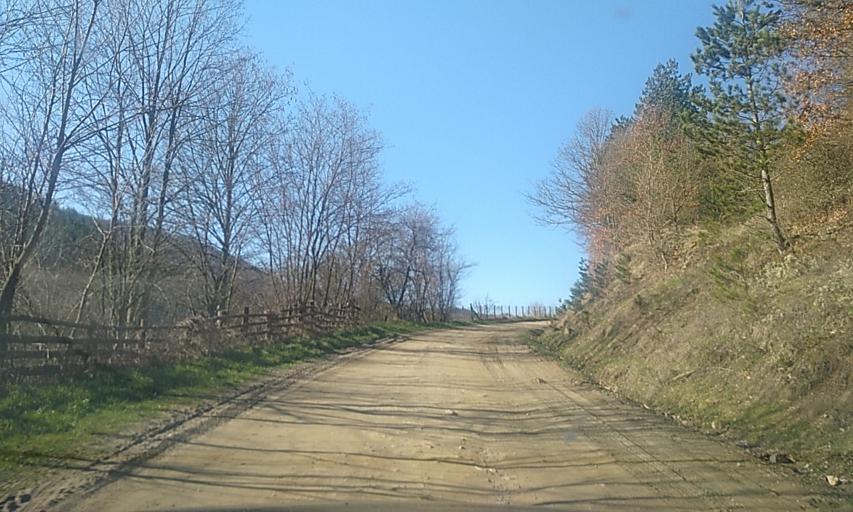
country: RS
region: Central Serbia
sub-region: Pcinjski Okrug
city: Bosilegrad
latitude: 42.3761
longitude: 22.4402
